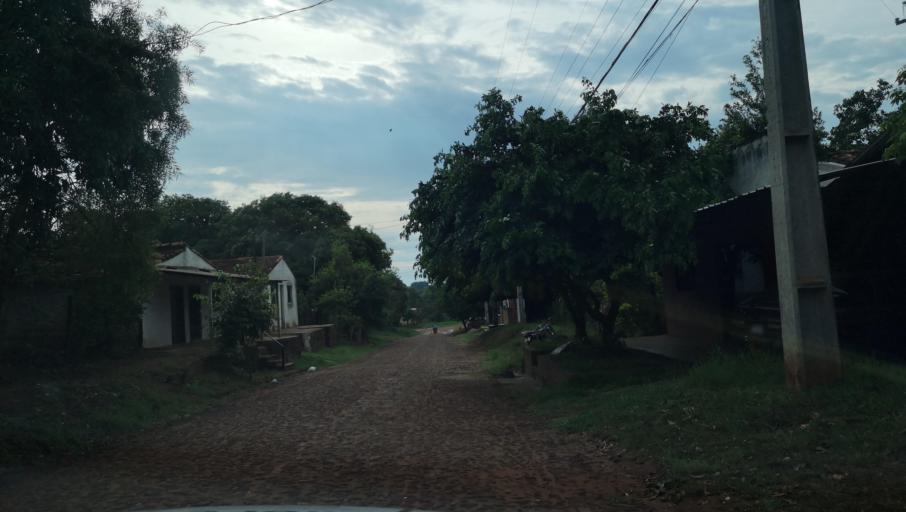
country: PY
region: Misiones
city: Santa Maria
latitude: -26.8816
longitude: -57.0248
